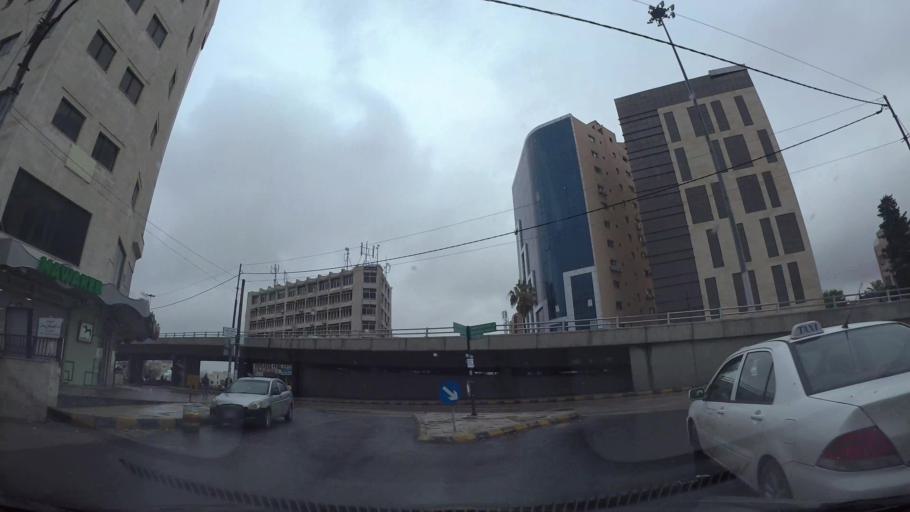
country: JO
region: Amman
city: Amman
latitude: 31.9718
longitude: 35.9109
